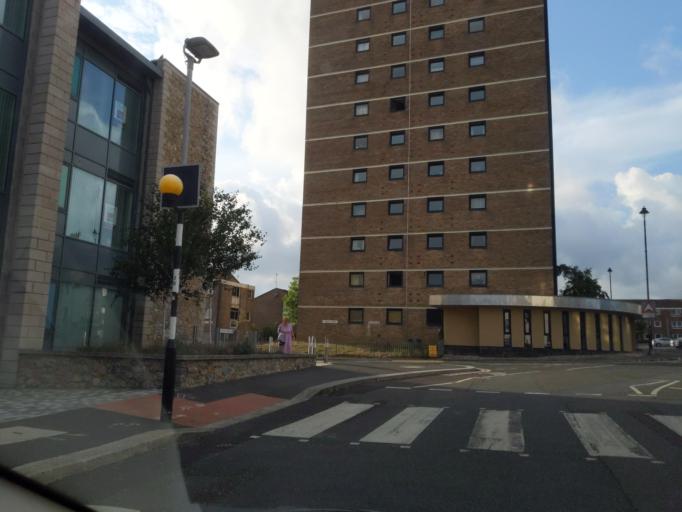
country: GB
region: England
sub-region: Cornwall
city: Millbrook
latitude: 50.3721
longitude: -4.1790
